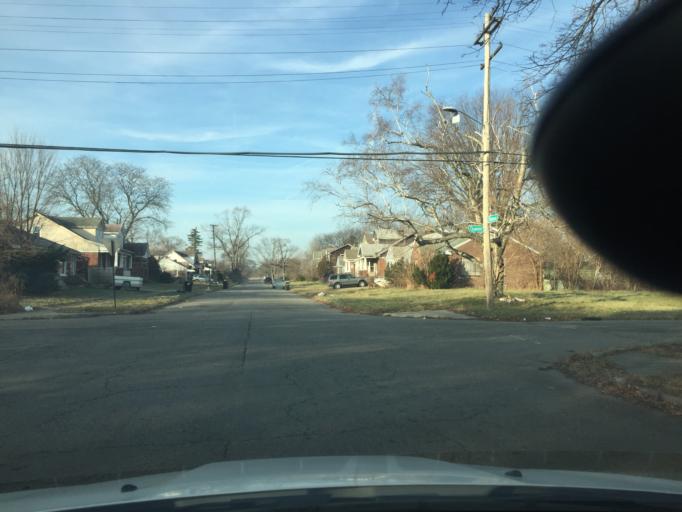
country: US
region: Michigan
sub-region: Macomb County
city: Eastpointe
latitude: 42.4394
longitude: -82.9685
